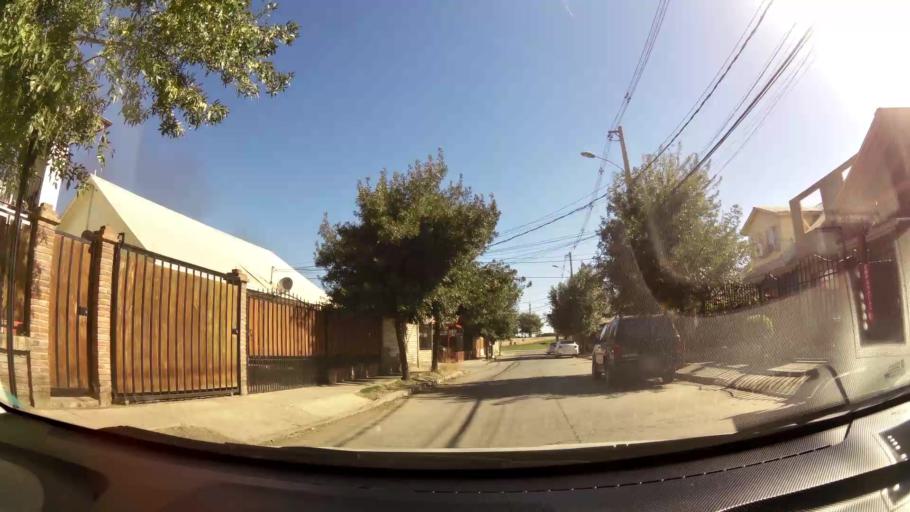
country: CL
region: O'Higgins
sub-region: Provincia de Cachapoal
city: Rancagua
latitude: -34.1836
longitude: -70.7741
